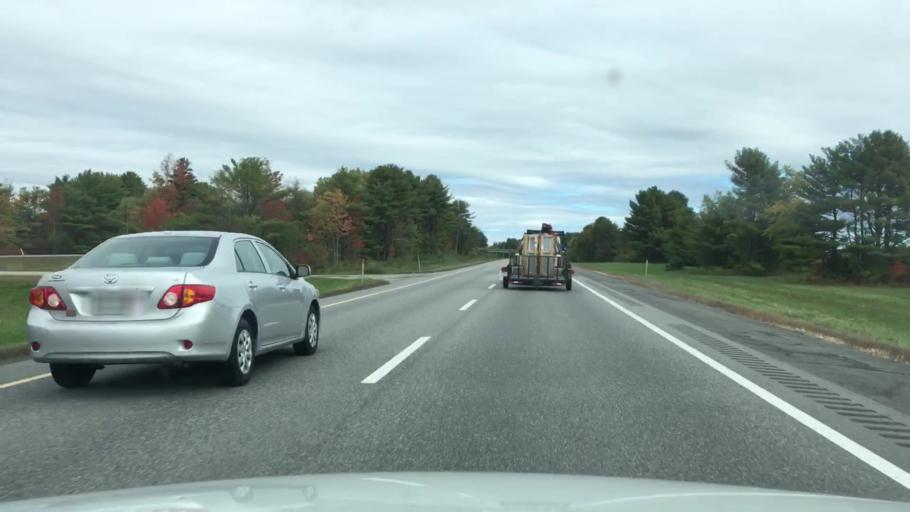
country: US
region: Maine
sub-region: Kennebec County
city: Sidney
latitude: 44.4487
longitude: -69.7192
